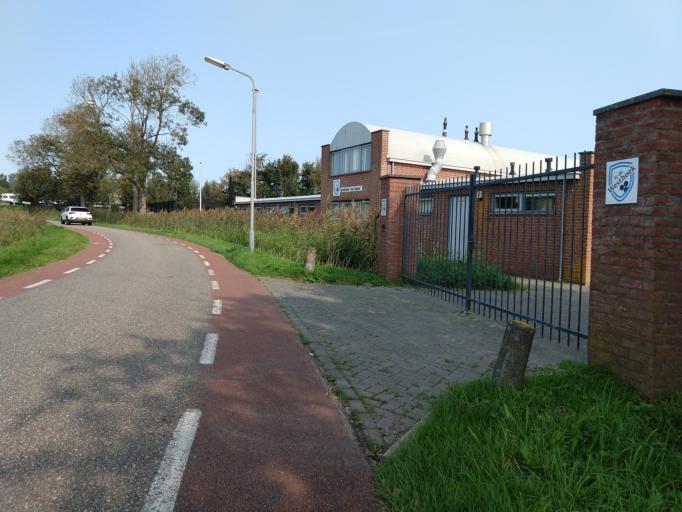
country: NL
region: Zeeland
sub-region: Schouwen-Duiveland
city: Burgh
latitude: 51.6907
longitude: 3.7380
